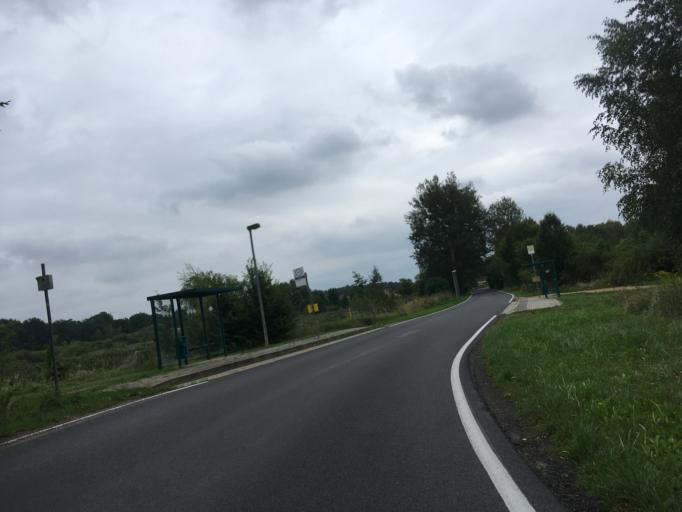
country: DE
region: Brandenburg
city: Zehdenick
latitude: 53.0501
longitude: 13.2939
